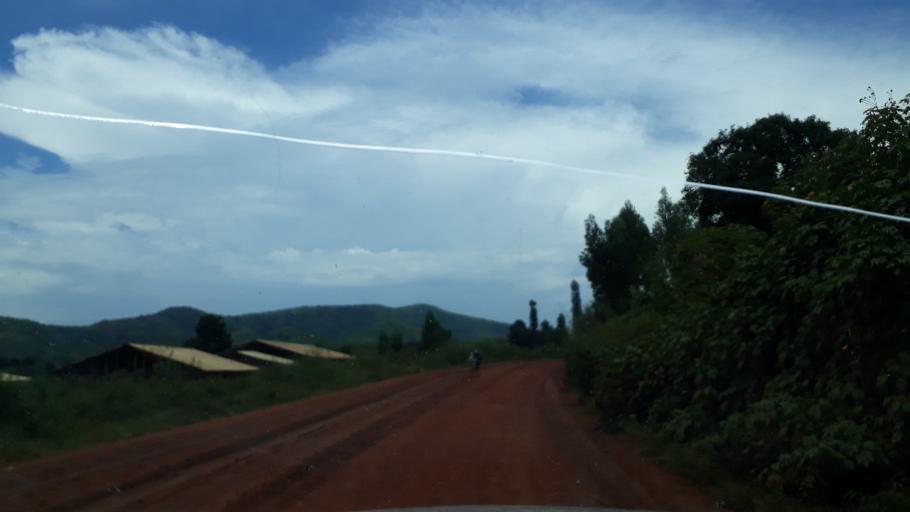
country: CD
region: Eastern Province
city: Bunia
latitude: 1.7030
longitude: 30.2867
